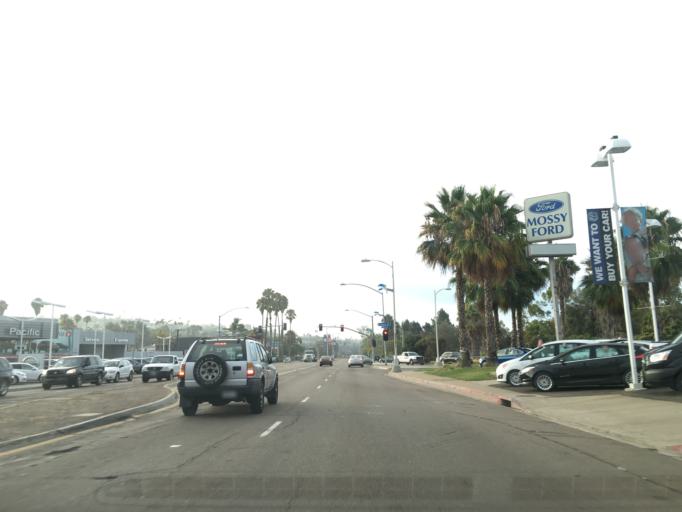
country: US
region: California
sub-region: San Diego County
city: La Jolla
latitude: 32.8026
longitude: -117.2162
